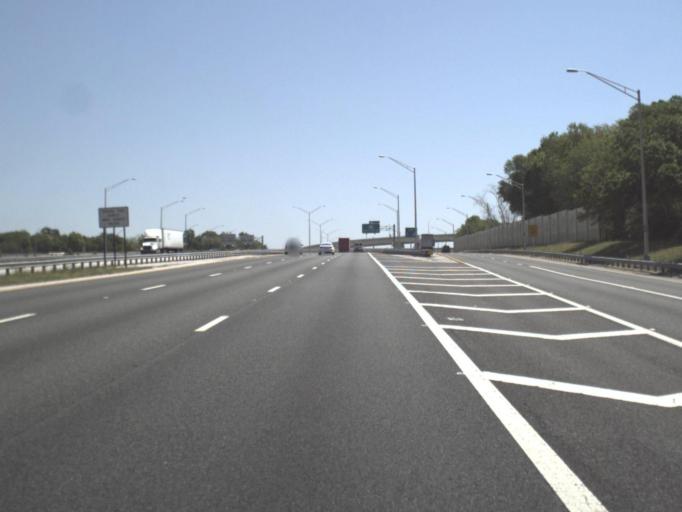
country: US
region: Florida
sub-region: Escambia County
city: Ferry Pass
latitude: 30.5034
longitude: -87.2363
